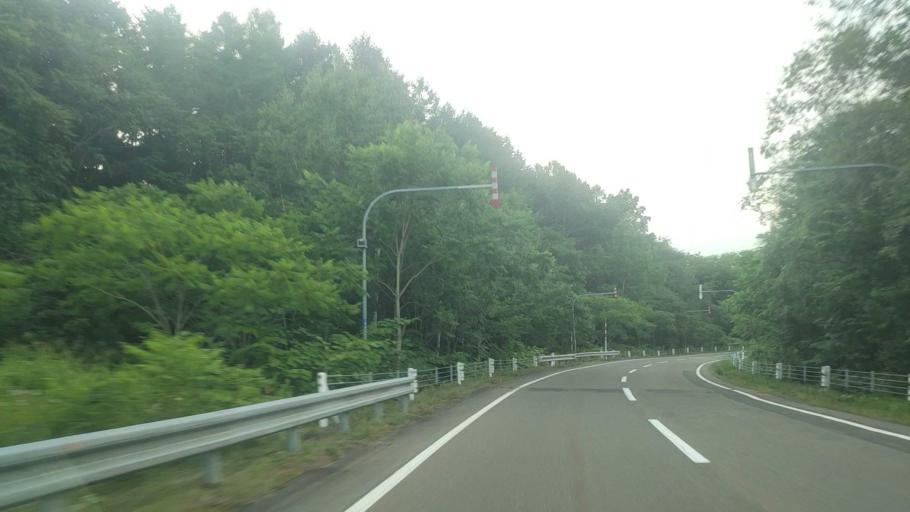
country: JP
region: Hokkaido
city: Bibai
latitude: 43.1255
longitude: 142.1018
